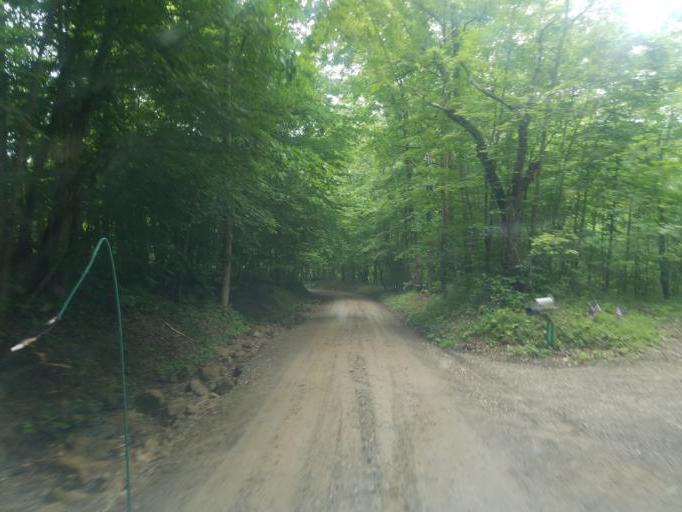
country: US
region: Ohio
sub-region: Knox County
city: Oak Hill
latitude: 40.3255
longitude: -82.1283
